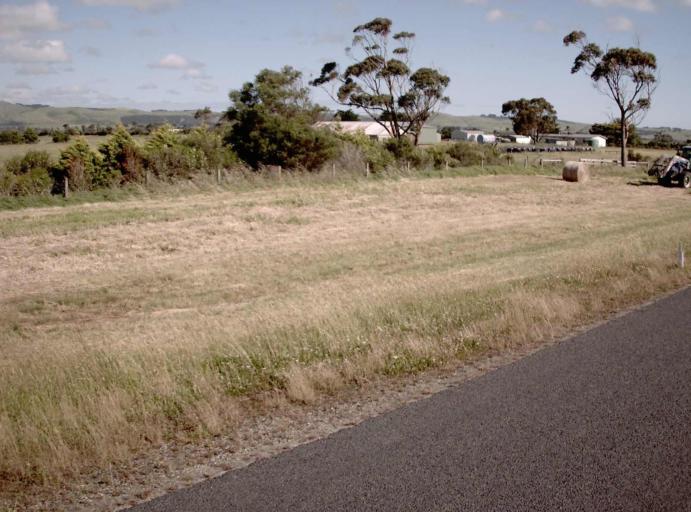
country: AU
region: Victoria
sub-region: Bass Coast
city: North Wonthaggi
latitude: -38.4507
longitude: 145.4817
